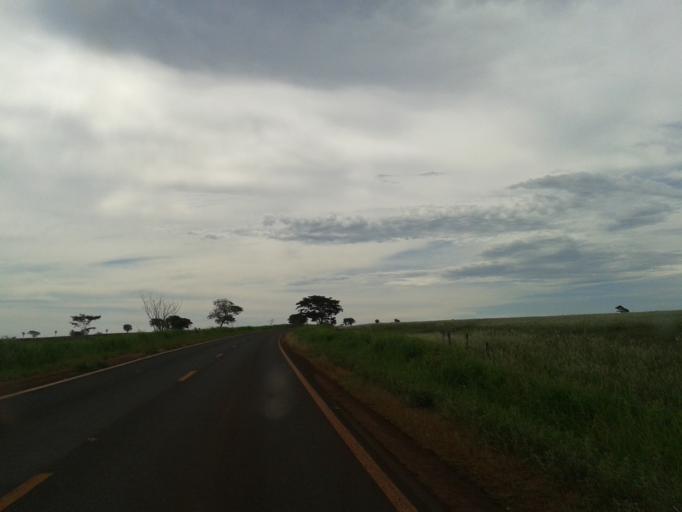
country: BR
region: Minas Gerais
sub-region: Capinopolis
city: Capinopolis
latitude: -18.6913
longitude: -49.3827
